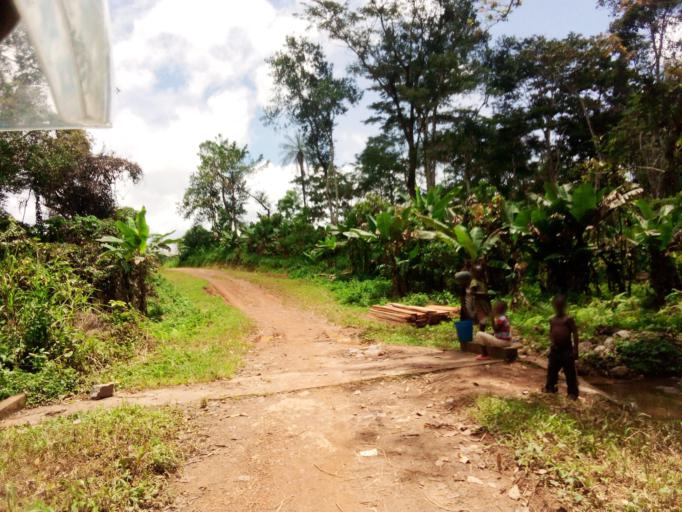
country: SL
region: Eastern Province
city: Giehun
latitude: 8.5575
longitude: -10.9868
